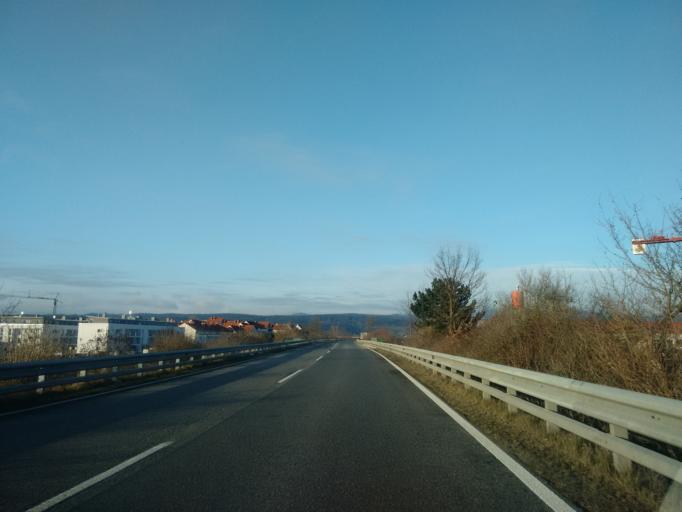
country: AT
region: Lower Austria
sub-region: Politischer Bezirk Melk
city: Melk
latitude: 48.2269
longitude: 15.3498
